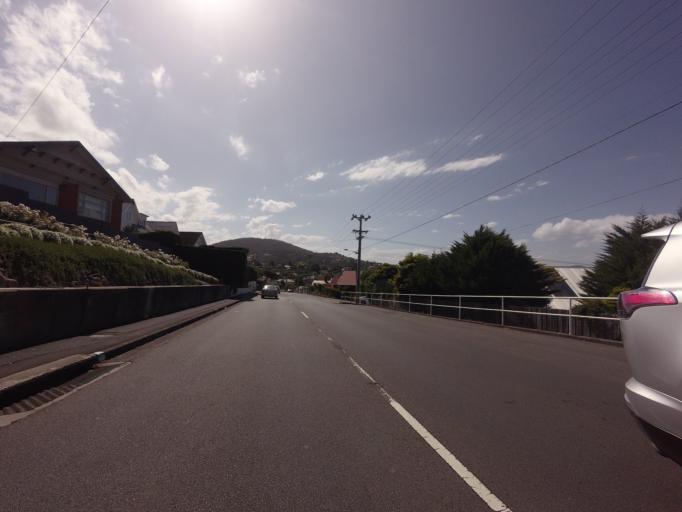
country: AU
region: Tasmania
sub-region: Hobart
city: Dynnyrne
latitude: -42.9025
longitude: 147.3190
